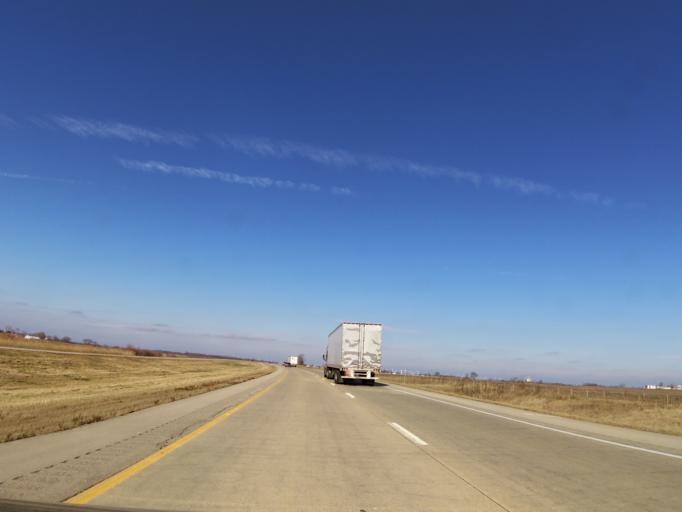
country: US
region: Illinois
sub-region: LaSalle County
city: Mendota
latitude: 41.5144
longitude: -89.0535
